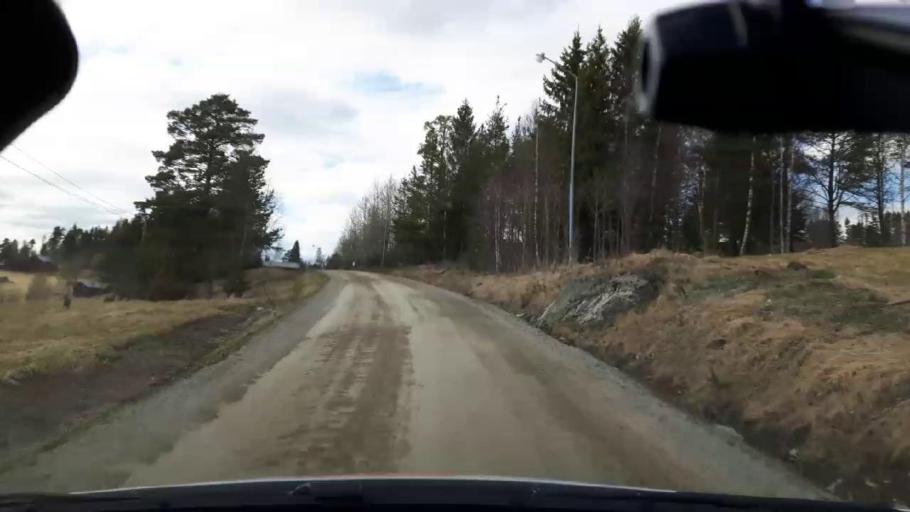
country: SE
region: Jaemtland
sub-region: Bergs Kommun
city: Hoverberg
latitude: 62.8811
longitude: 14.6665
